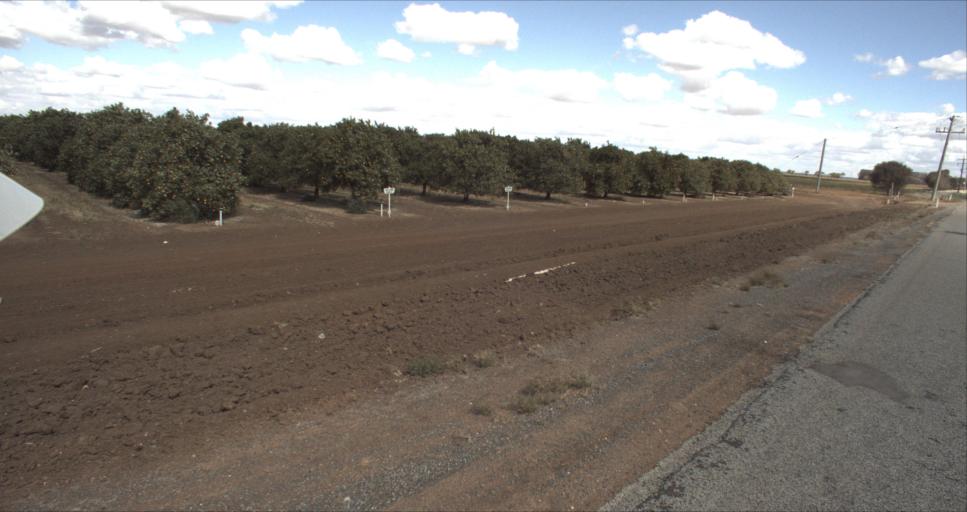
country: AU
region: New South Wales
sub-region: Leeton
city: Leeton
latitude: -34.5238
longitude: 146.2224
